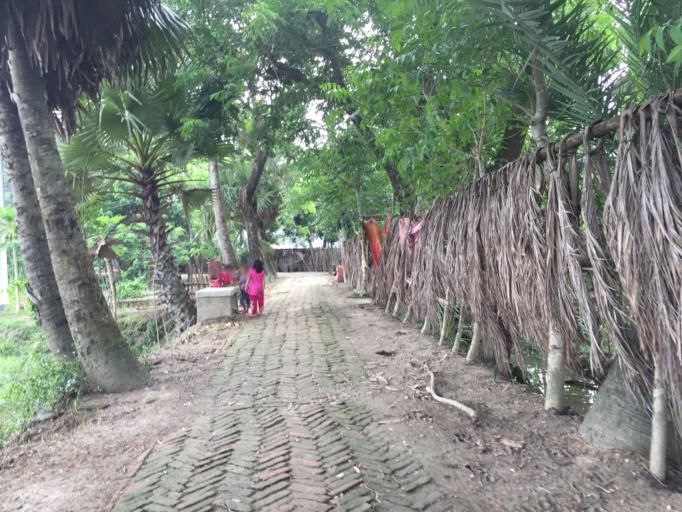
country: BD
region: Barisal
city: Mathba
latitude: 22.1893
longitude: 89.9286
